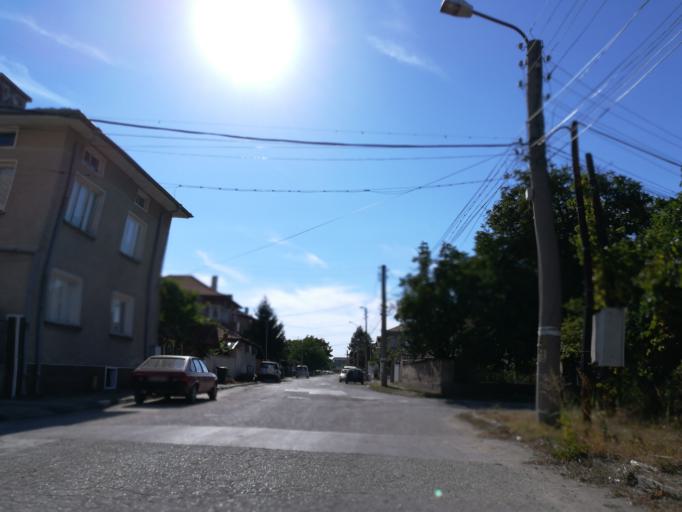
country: BG
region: Stara Zagora
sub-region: Obshtina Chirpan
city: Chirpan
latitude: 42.0939
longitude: 25.2280
